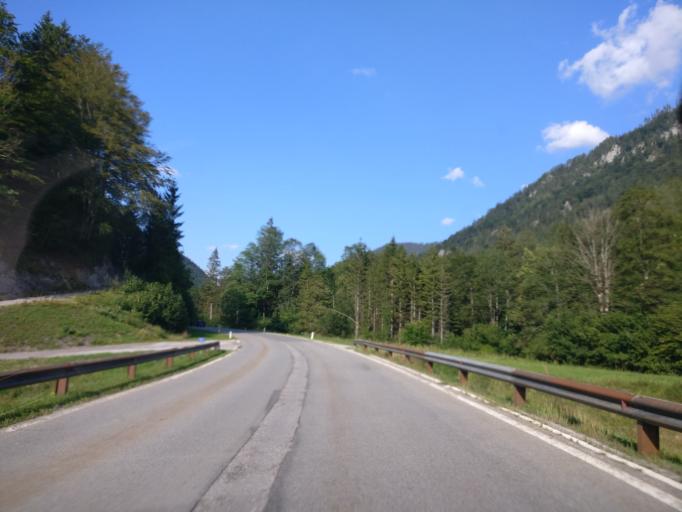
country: AT
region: Styria
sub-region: Politischer Bezirk Liezen
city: Palfau
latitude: 47.7213
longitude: 14.8461
